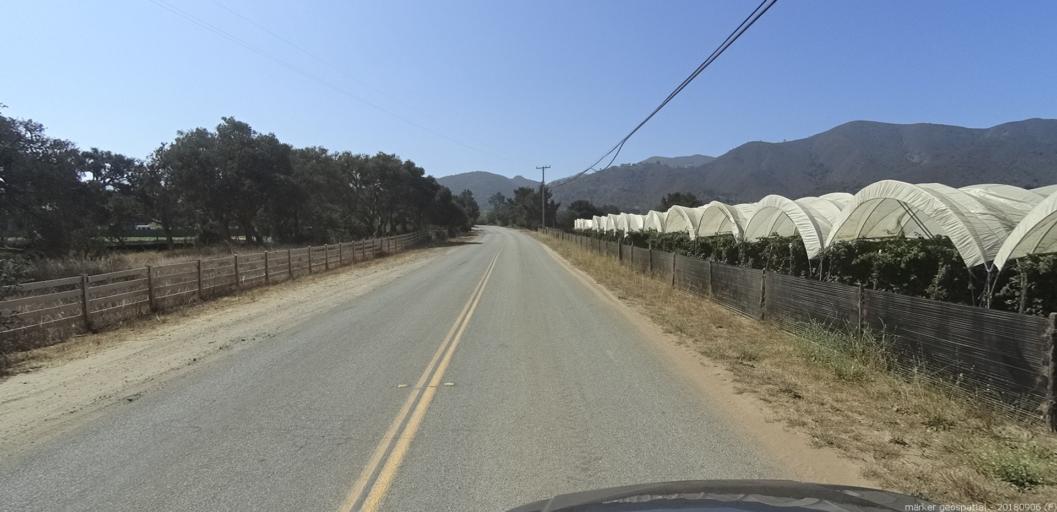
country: US
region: California
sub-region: Monterey County
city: Salinas
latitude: 36.5902
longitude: -121.6292
